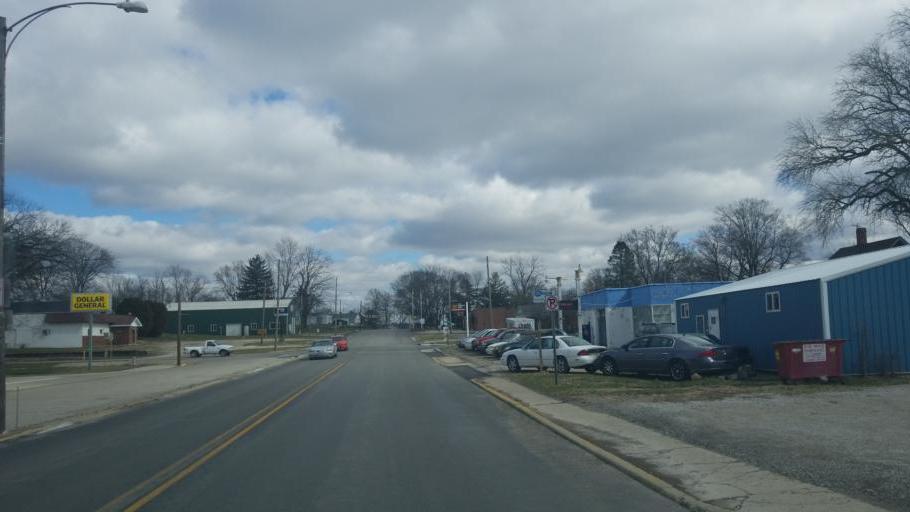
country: US
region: Indiana
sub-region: Parke County
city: Montezuma
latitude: 39.7928
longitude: -87.3719
